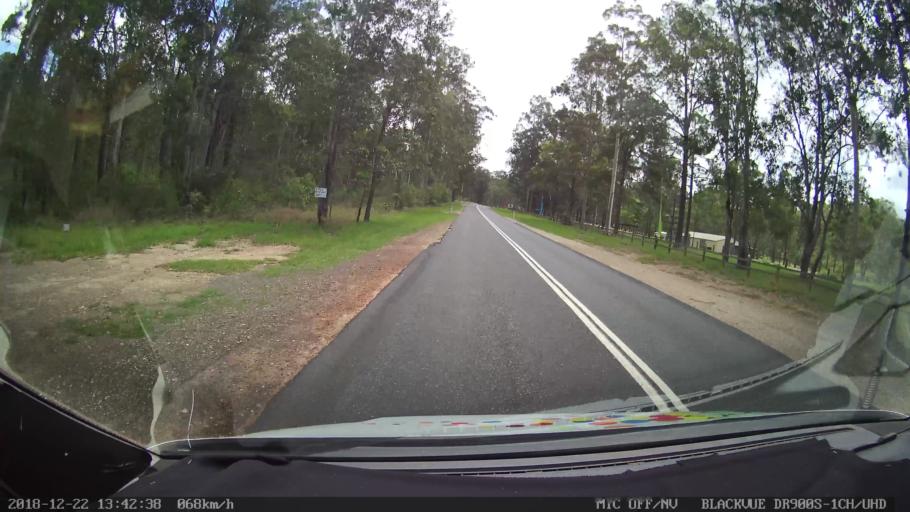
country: AU
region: New South Wales
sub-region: Clarence Valley
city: Coutts Crossing
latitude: -29.9246
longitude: 152.7513
